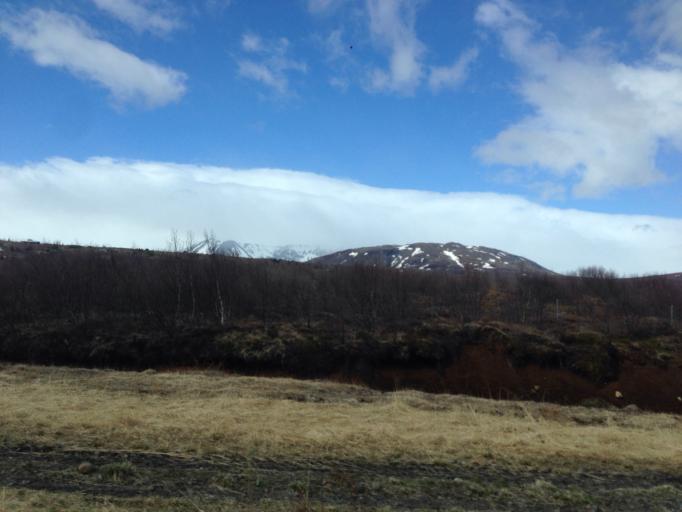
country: IS
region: South
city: Selfoss
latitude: 64.2767
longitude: -20.4317
